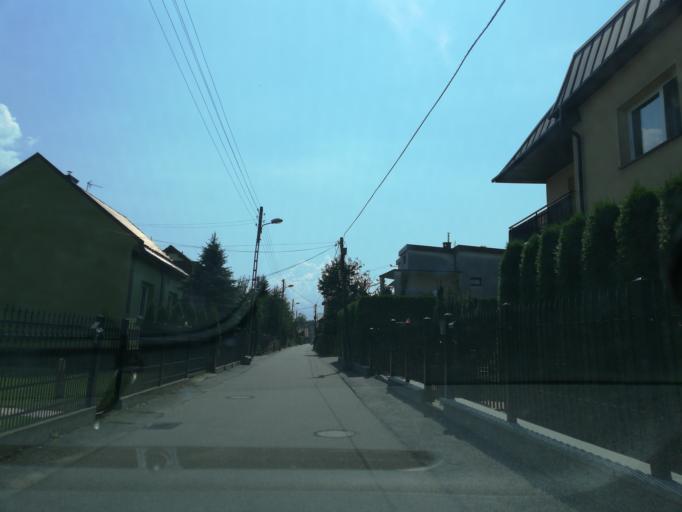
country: PL
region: Lesser Poland Voivodeship
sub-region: Powiat nowosadecki
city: Chelmiec
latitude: 49.6316
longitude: 20.6789
